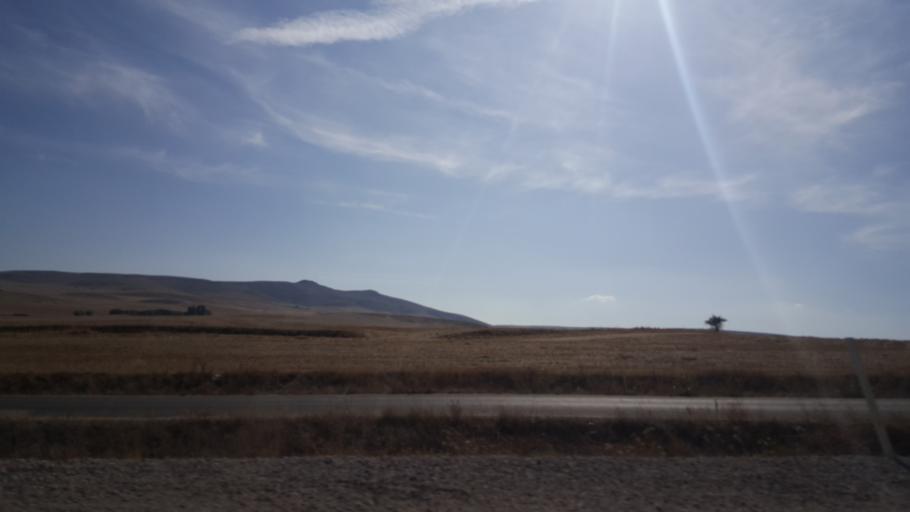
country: TR
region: Ankara
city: Yenice
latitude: 39.3647
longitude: 32.6817
